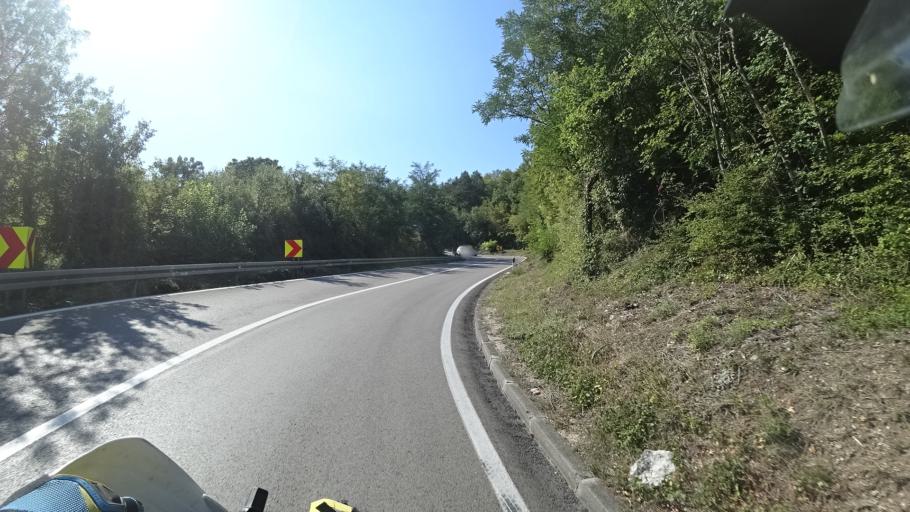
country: HR
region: Sibensko-Kniniska
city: Knin
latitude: 44.0169
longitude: 16.1959
